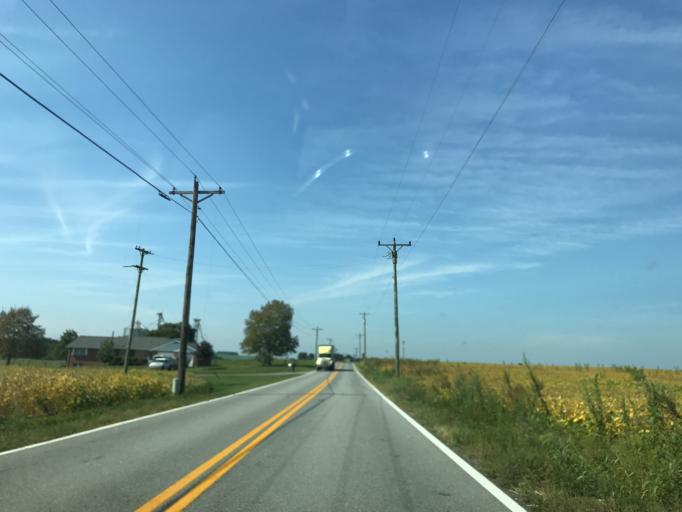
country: US
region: Maryland
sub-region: Queen Anne's County
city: Kingstown
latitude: 39.2741
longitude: -75.9484
